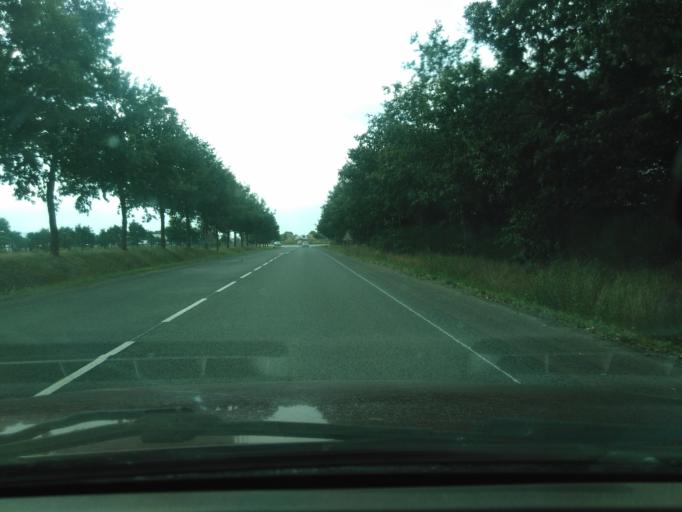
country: FR
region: Pays de la Loire
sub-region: Departement de la Vendee
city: Belleville-sur-Vie
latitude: 46.7449
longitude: -1.4236
